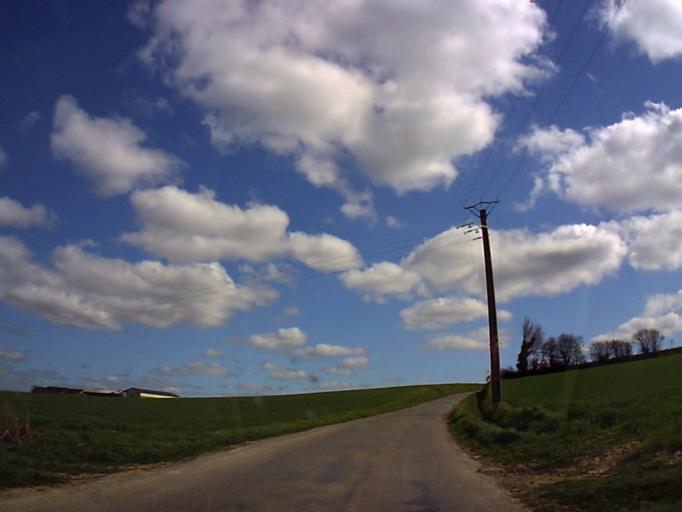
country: FR
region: Brittany
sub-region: Departement d'Ille-et-Vilaine
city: Boisgervilly
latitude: 48.1023
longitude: -2.1190
